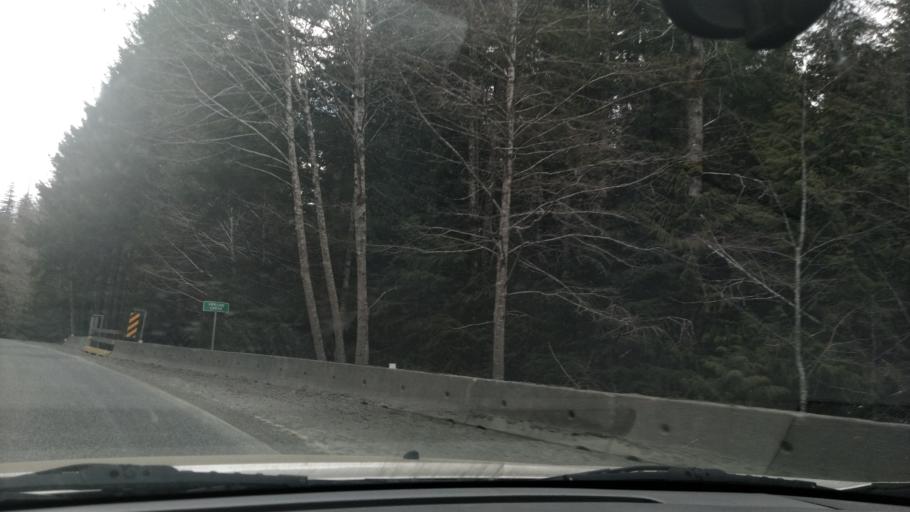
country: CA
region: British Columbia
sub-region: Regional District of Alberni-Clayoquot
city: Tofino
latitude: 49.8399
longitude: -125.9299
